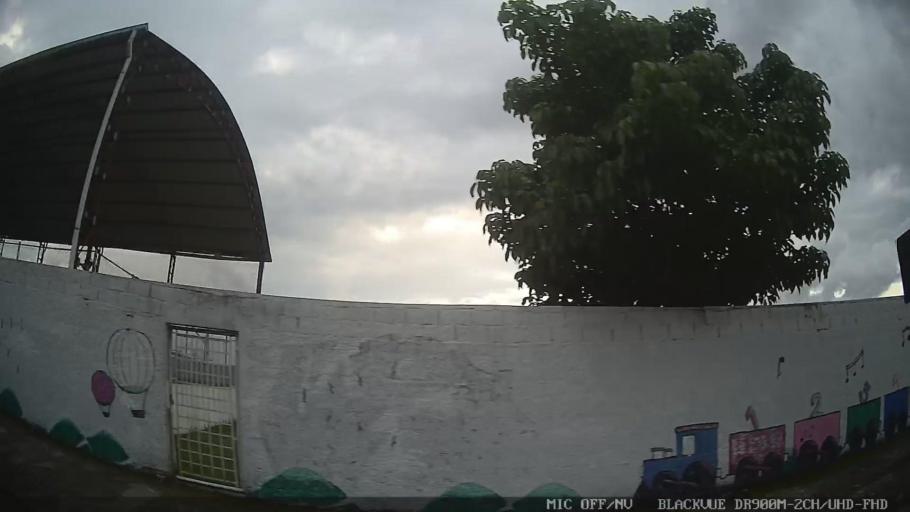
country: BR
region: Sao Paulo
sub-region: Mogi das Cruzes
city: Mogi das Cruzes
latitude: -23.5487
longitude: -46.1979
